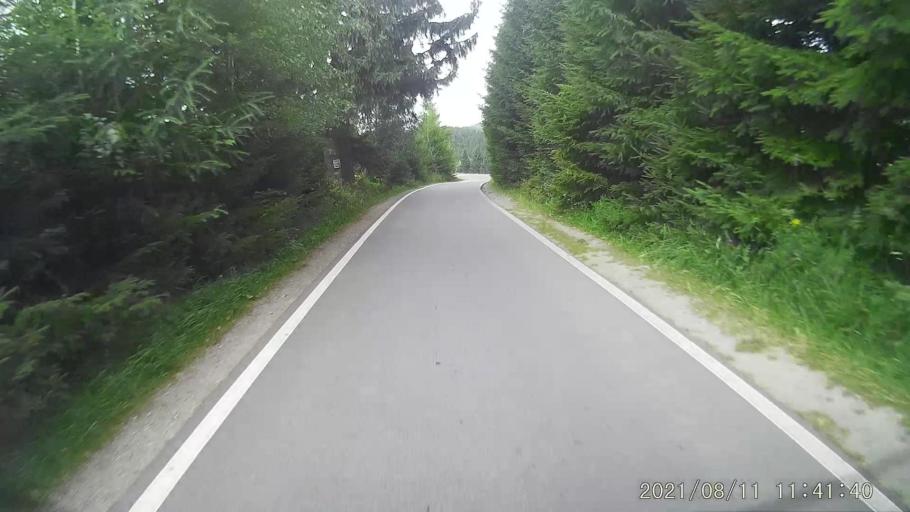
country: PL
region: Lower Silesian Voivodeship
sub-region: Powiat klodzki
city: Stronie Slaskie
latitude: 50.2542
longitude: 16.8382
